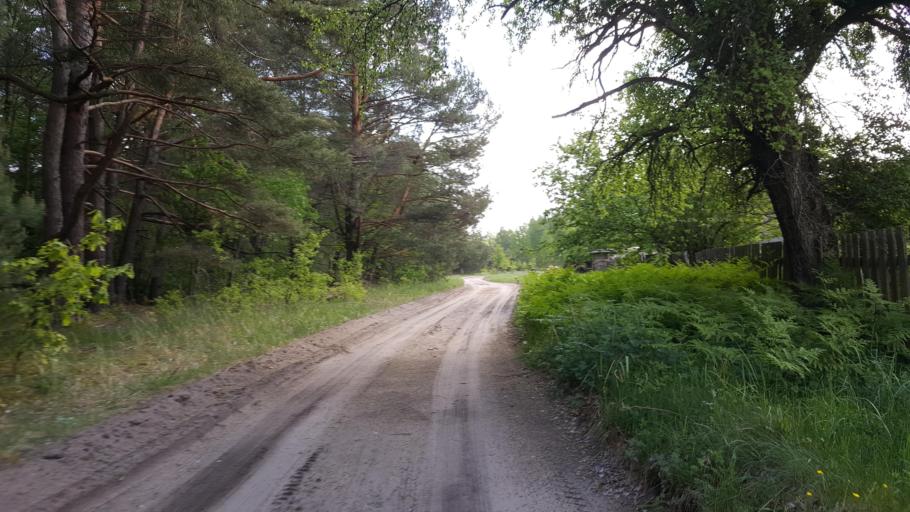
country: BY
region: Brest
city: Kamyanyuki
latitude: 52.4910
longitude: 23.9611
